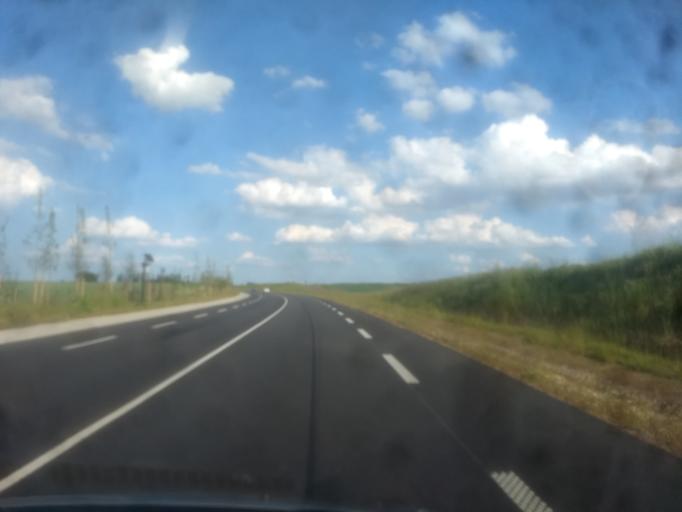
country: FR
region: Nord-Pas-de-Calais
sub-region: Departement du Pas-de-Calais
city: Agny
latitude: 50.2527
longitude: 2.7487
